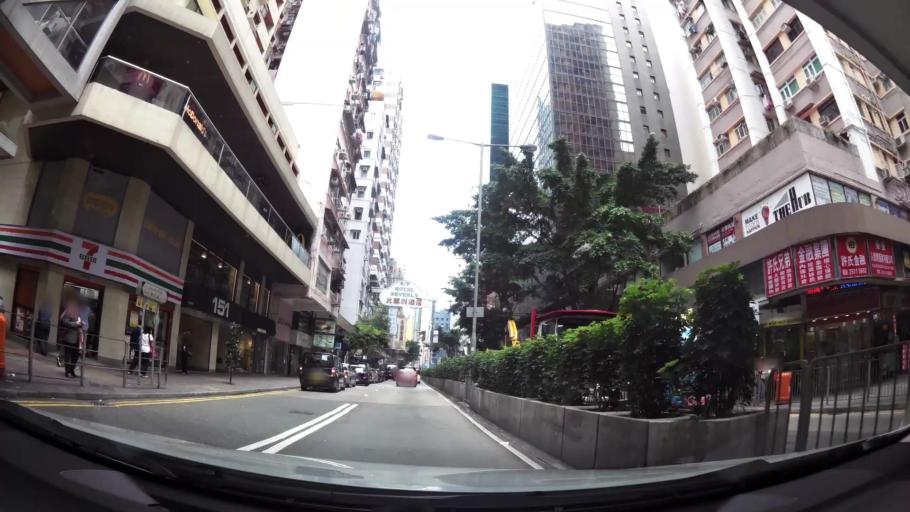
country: HK
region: Wanchai
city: Wan Chai
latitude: 22.2784
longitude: 114.1728
